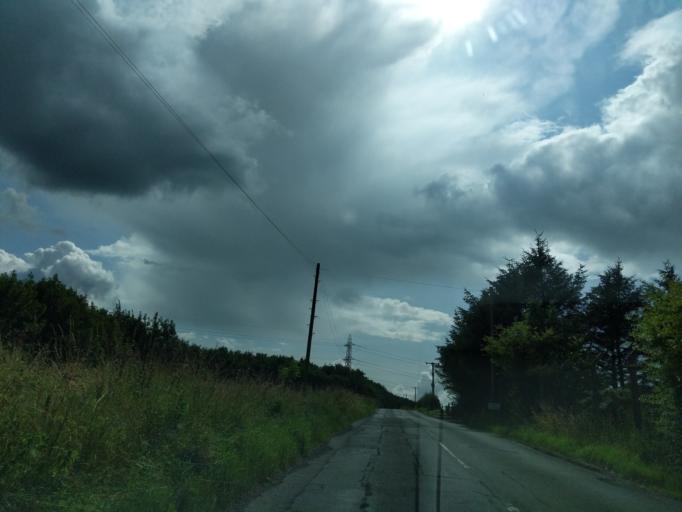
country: GB
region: Scotland
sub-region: East Renfrewshire
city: Neilston
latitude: 55.7753
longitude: -4.4320
